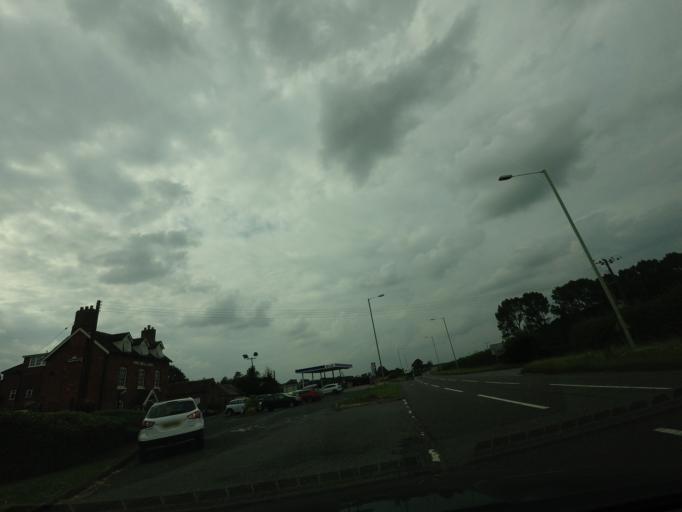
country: GB
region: England
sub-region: Shropshire
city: Tong
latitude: 52.6699
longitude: -2.3093
